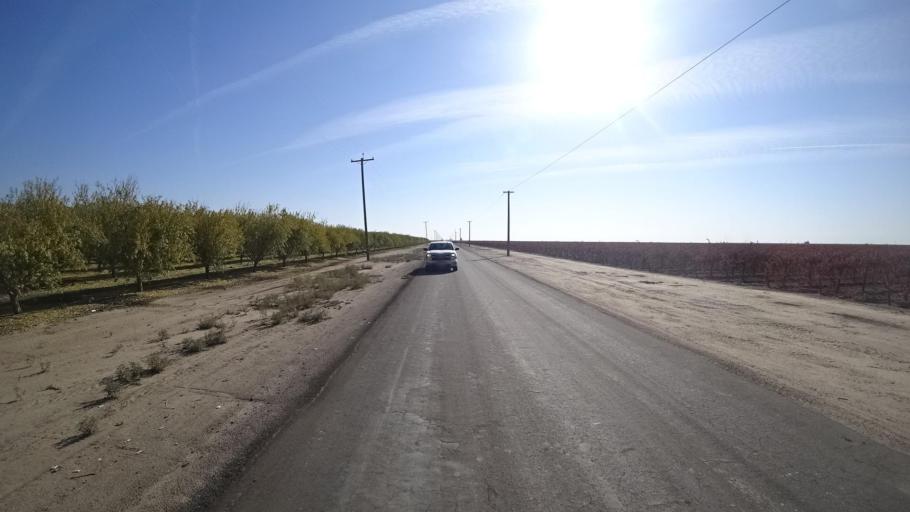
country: US
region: California
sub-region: Kern County
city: Wasco
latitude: 35.7022
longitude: -119.3838
